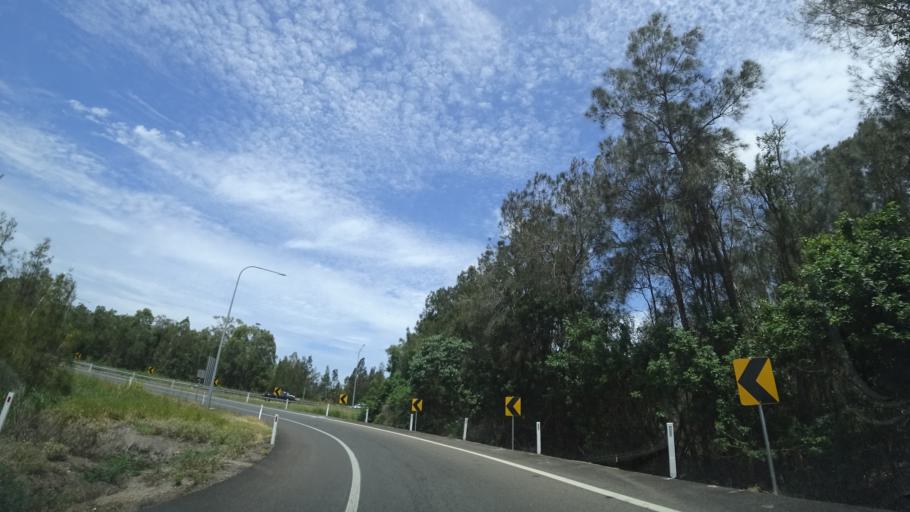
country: AU
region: Queensland
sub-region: Sunshine Coast
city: Buderim
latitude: -26.6462
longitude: 153.0656
